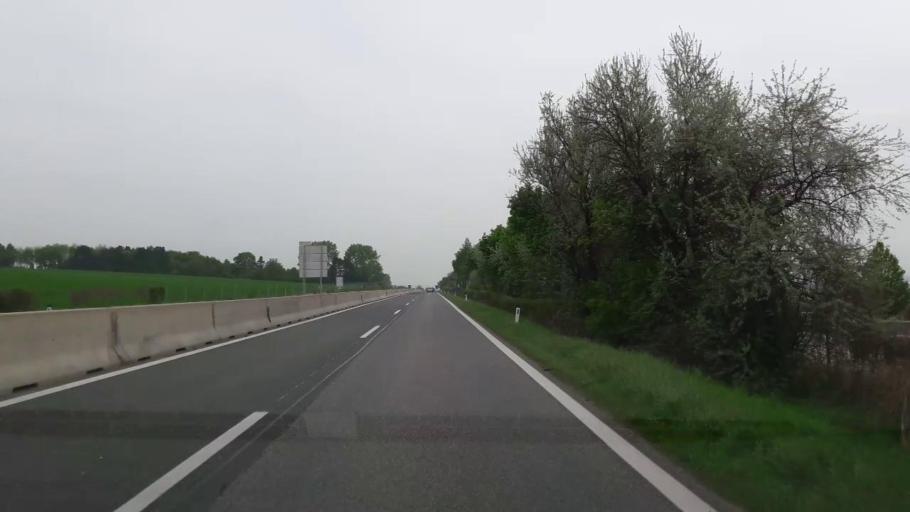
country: AT
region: Lower Austria
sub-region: Politischer Bezirk Korneuburg
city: Sierndorf
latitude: 48.4440
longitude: 16.1633
